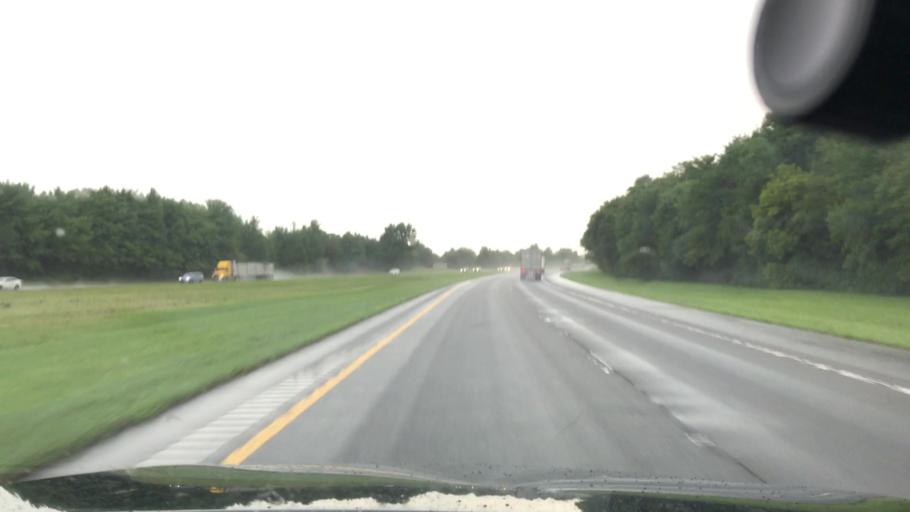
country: US
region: North Carolina
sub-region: Iredell County
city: Statesville
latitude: 35.9317
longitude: -80.8554
